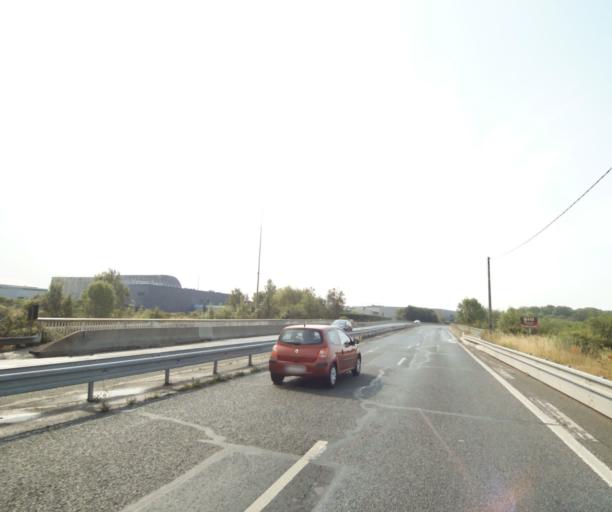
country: FR
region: Ile-de-France
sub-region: Departement du Val-d'Oise
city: Neuville-sur-Oise
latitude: 49.0070
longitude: 2.0741
